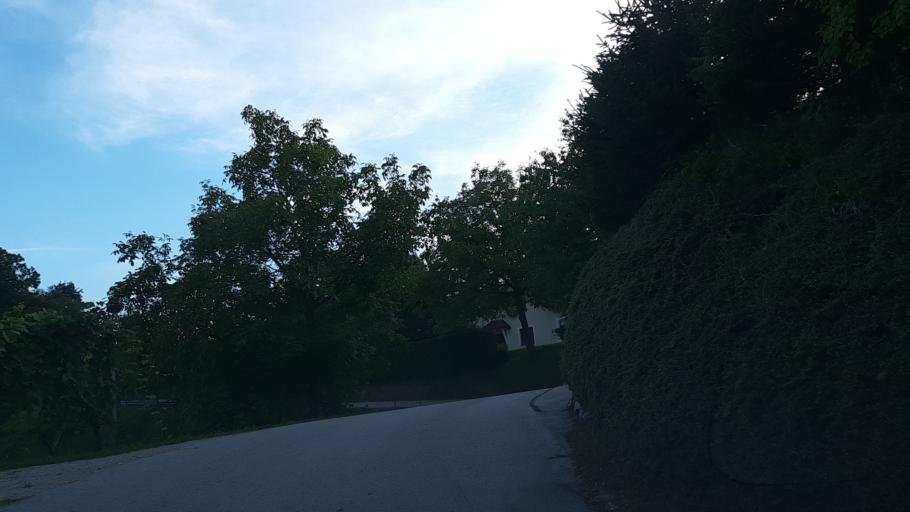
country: SI
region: Dobje
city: Dobje pri Planini
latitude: 46.1457
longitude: 15.4541
